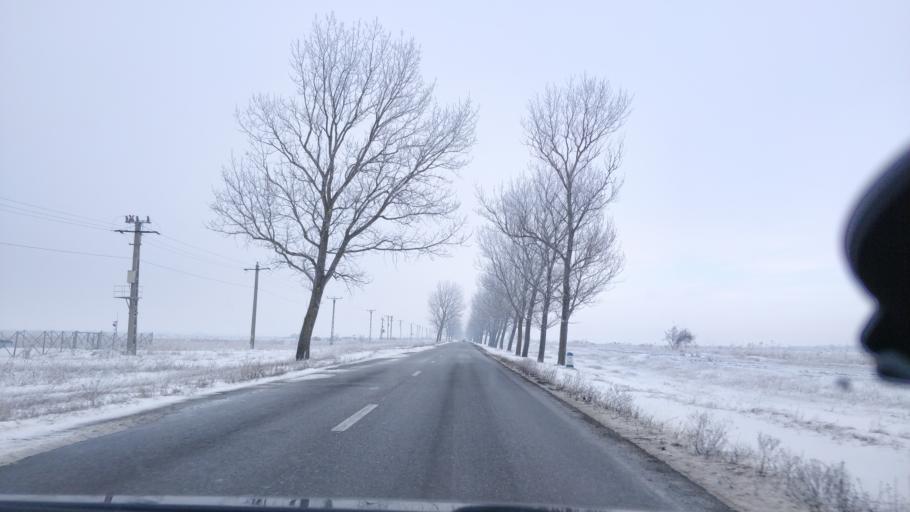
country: RO
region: Vrancea
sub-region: Comuna Vanatori
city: Jorasti
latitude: 45.6976
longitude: 27.2411
